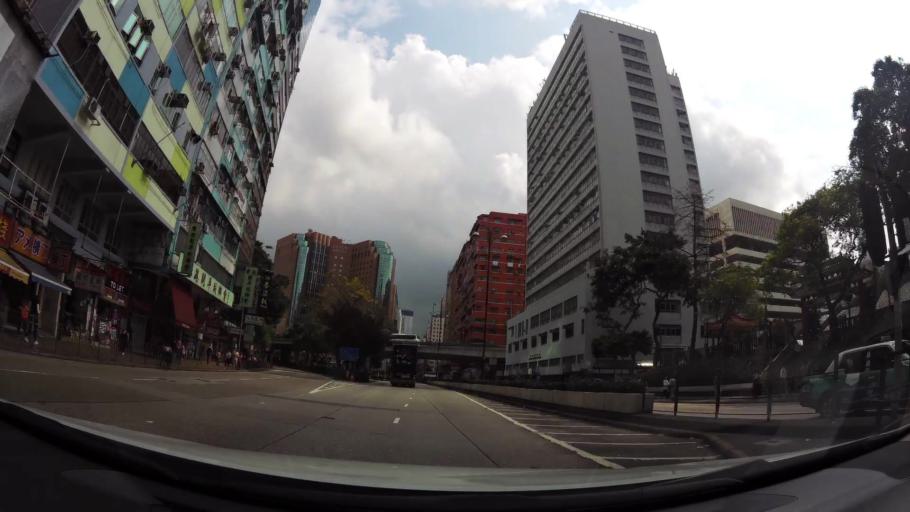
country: HK
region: Kowloon City
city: Kowloon
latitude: 22.3101
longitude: 114.1712
